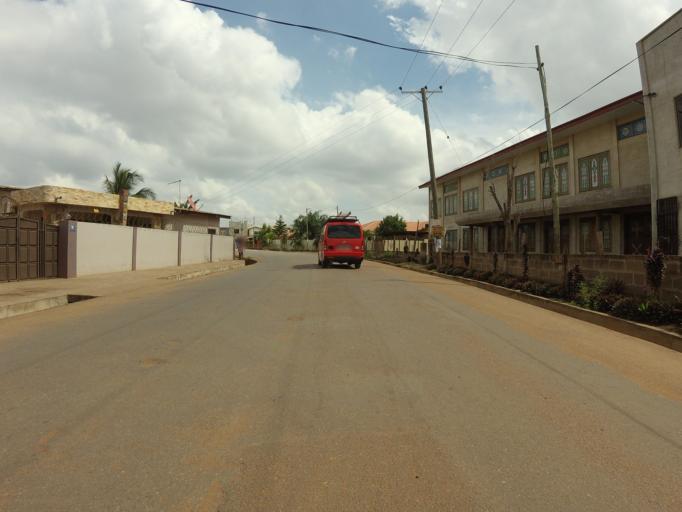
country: GH
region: Greater Accra
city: Nungua
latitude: 5.6255
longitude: -0.0927
